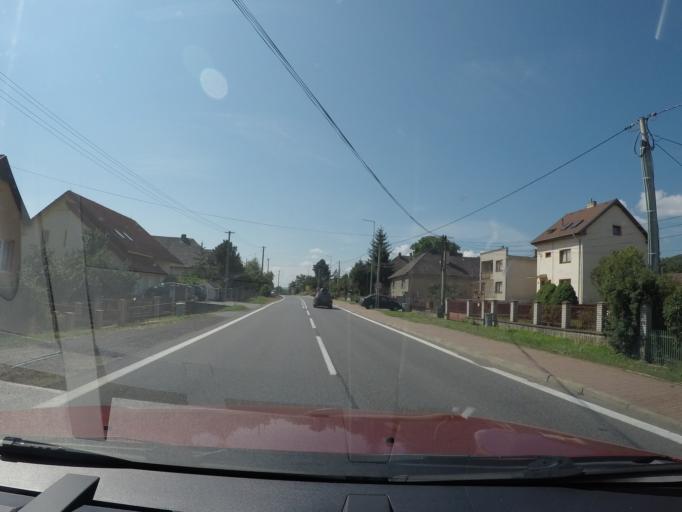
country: SK
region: Presovsky
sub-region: Okres Presov
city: Presov
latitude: 48.9280
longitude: 21.2412
